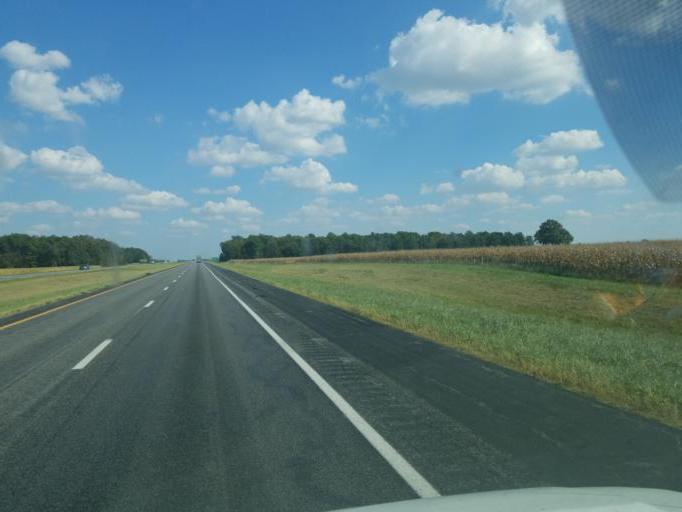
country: US
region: Ohio
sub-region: Hardin County
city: Ada
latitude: 40.8266
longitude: -83.8005
